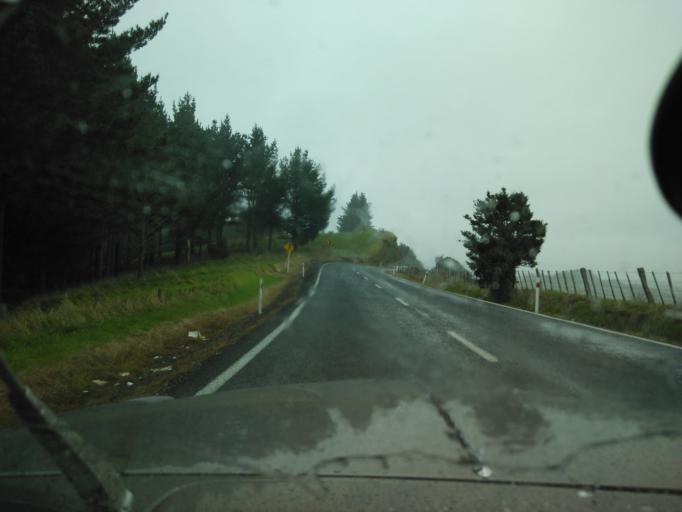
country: NZ
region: Auckland
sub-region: Auckland
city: Wellsford
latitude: -36.3599
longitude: 174.4647
